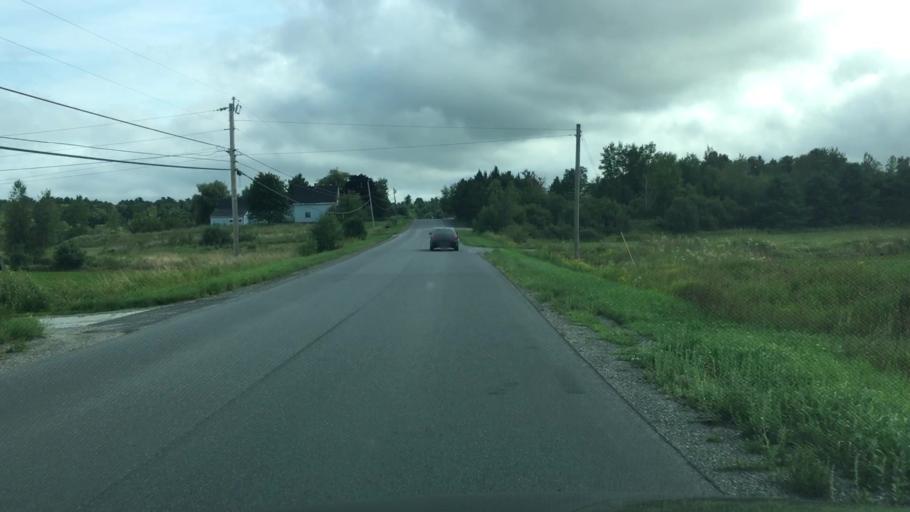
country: US
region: Maine
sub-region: Waldo County
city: Winterport
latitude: 44.6727
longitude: -68.8684
